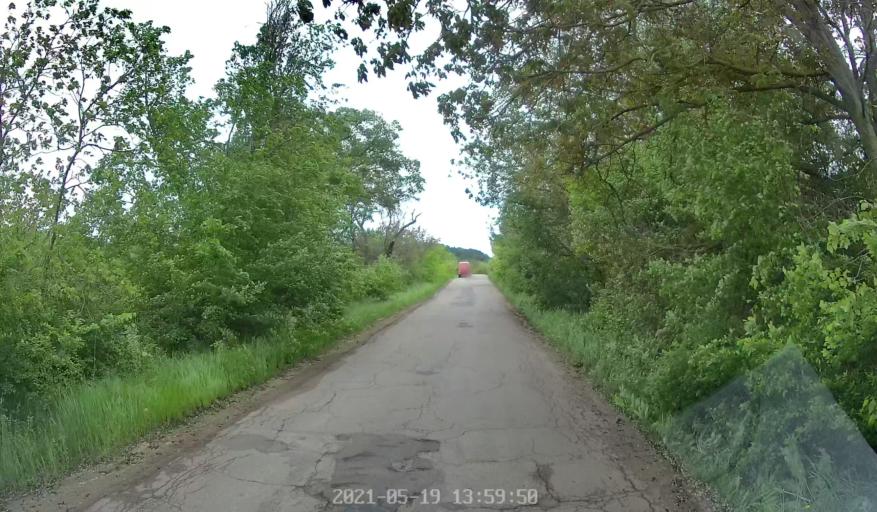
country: MD
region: Chisinau
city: Chisinau
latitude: 47.0382
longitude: 28.9270
